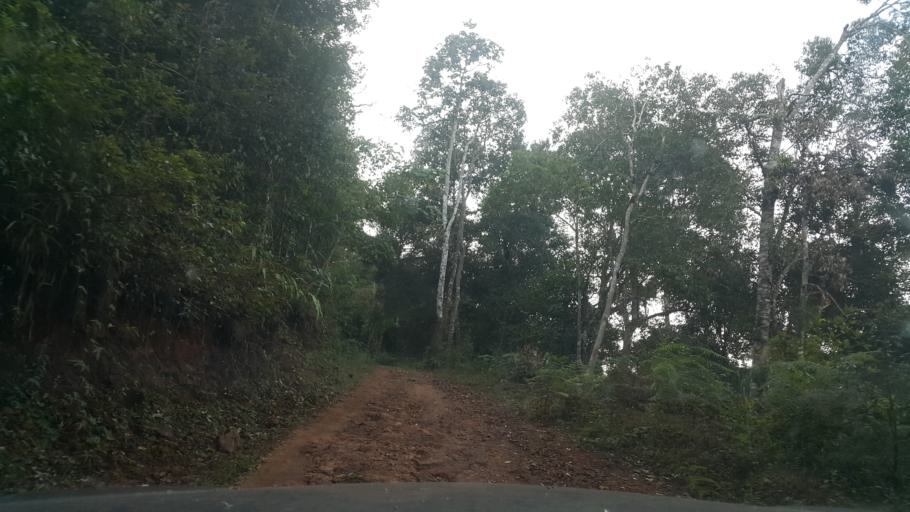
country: TH
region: Chiang Mai
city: Samoeng
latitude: 19.0314
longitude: 98.6482
